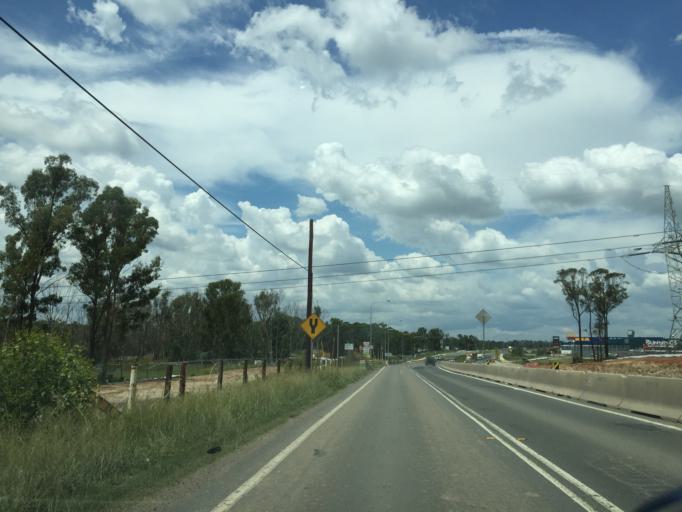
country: AU
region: New South Wales
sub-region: Blacktown
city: Hassall Grove
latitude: -33.7126
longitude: 150.8424
